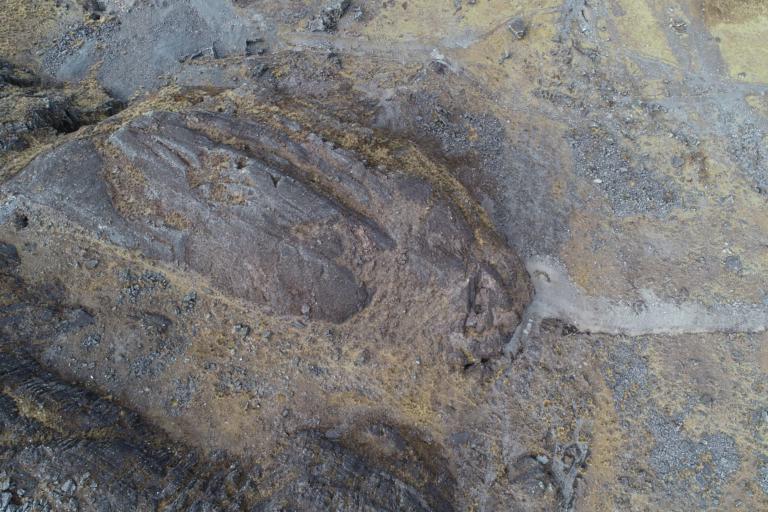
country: BO
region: La Paz
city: Sorata
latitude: -15.6688
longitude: -68.5523
